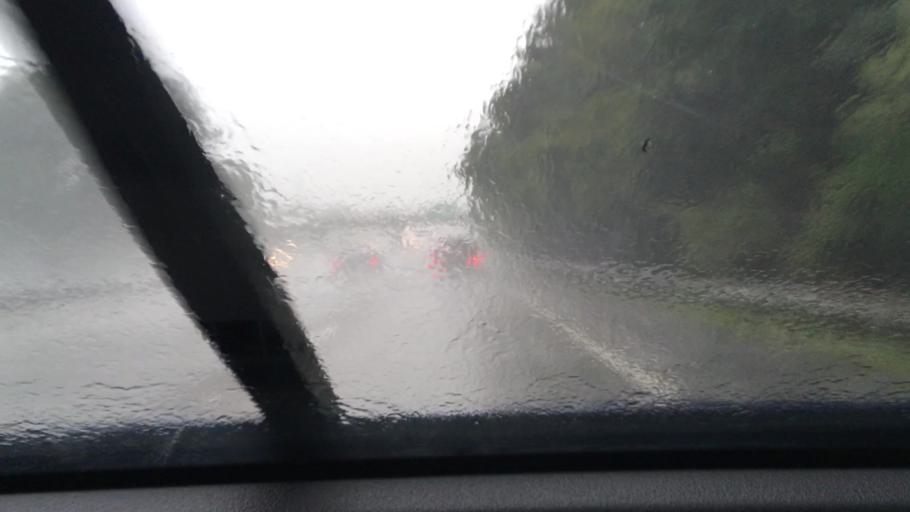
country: US
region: South Carolina
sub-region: Richland County
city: Dentsville
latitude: 34.0740
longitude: -80.9568
